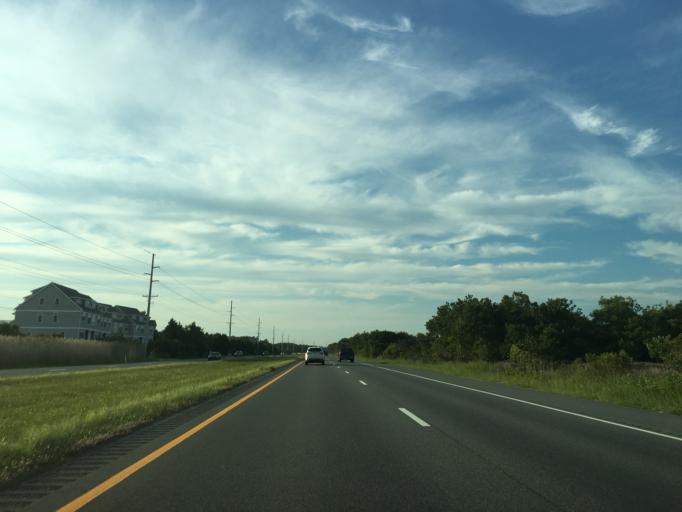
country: US
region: Delaware
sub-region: Sussex County
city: Bethany Beach
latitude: 38.4895
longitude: -75.0534
